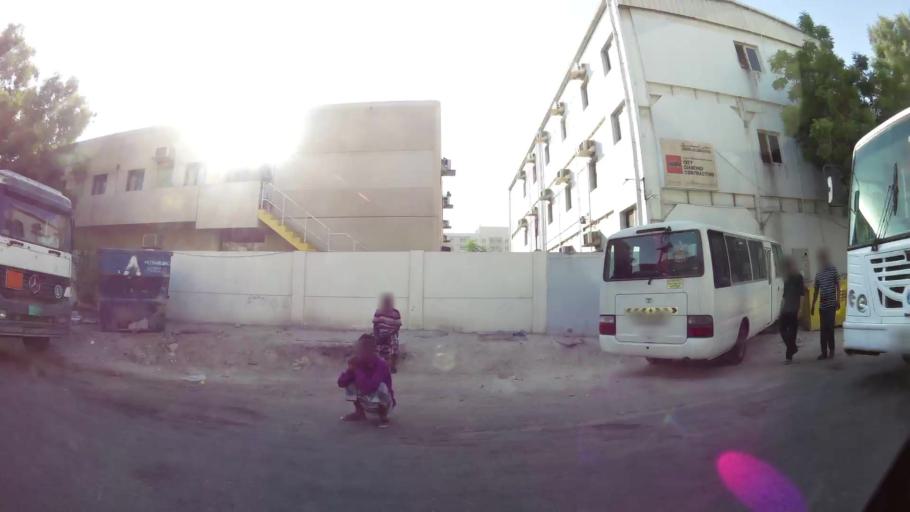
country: AE
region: Dubai
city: Dubai
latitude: 25.1362
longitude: 55.2565
